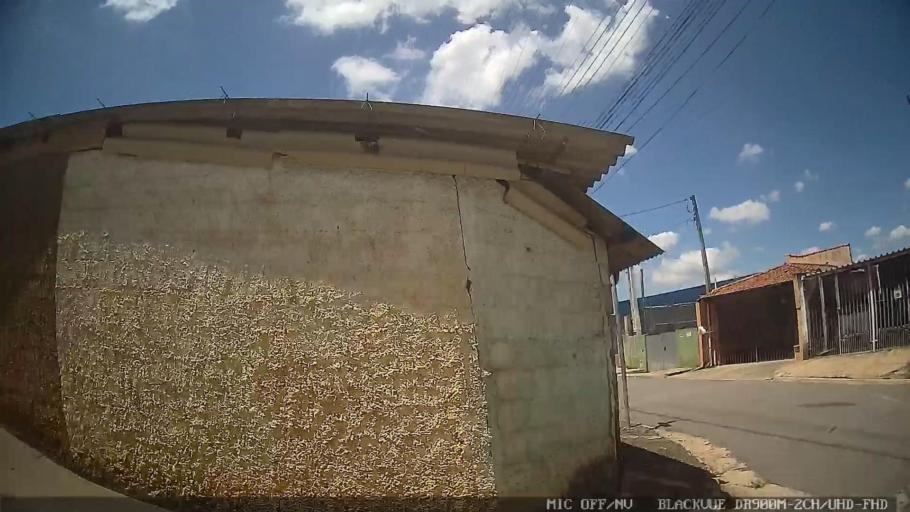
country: BR
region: Sao Paulo
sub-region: Atibaia
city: Atibaia
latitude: -23.1011
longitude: -46.5561
